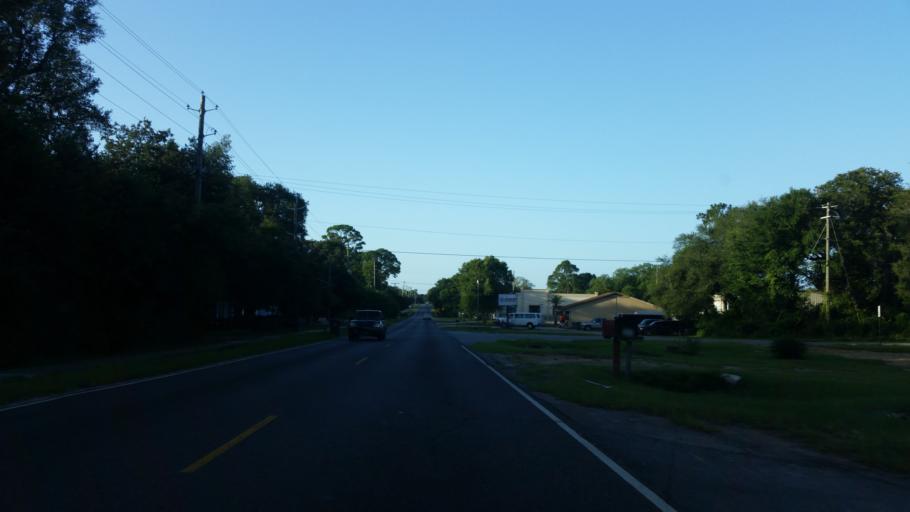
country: US
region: Florida
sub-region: Escambia County
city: Warrington
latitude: 30.4013
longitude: -87.2740
